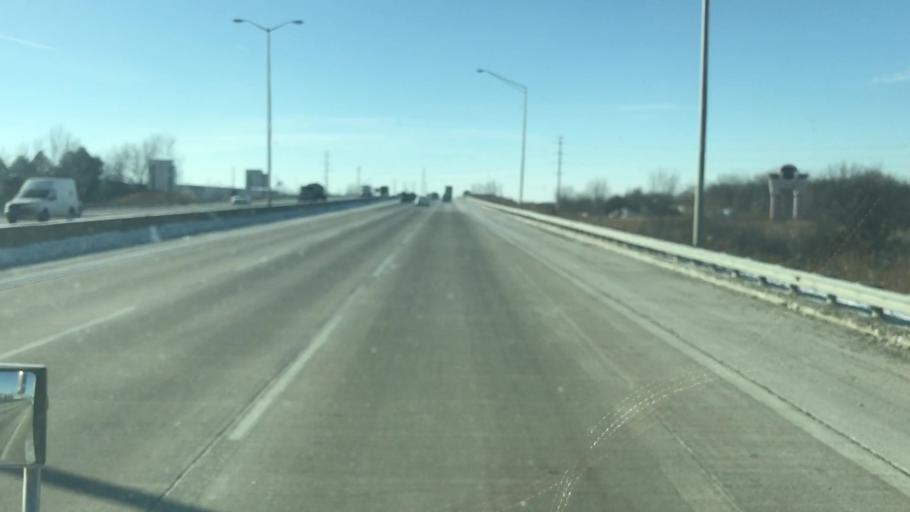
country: US
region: Illinois
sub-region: DuPage County
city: Warrenville
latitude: 41.8032
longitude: -88.2110
